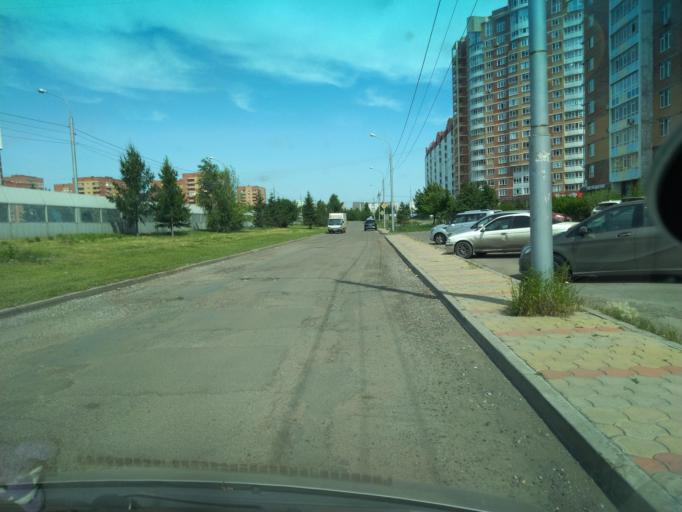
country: RU
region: Krasnoyarskiy
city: Krasnoyarsk
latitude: 56.0529
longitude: 92.9166
